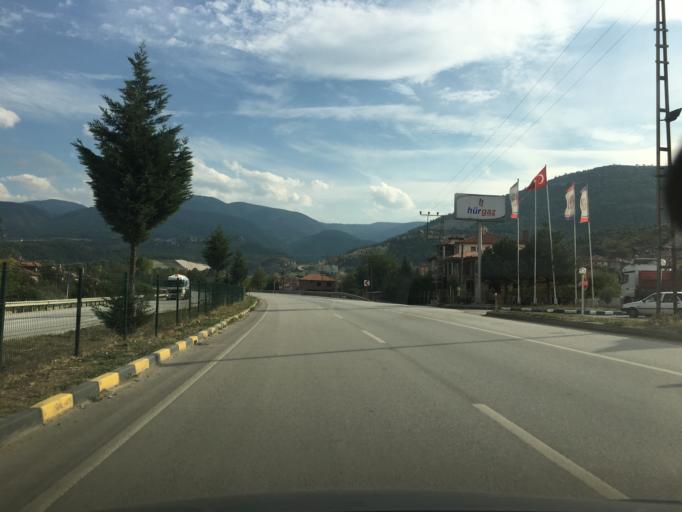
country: TR
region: Karabuk
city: Karabuk
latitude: 41.1036
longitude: 32.6691
